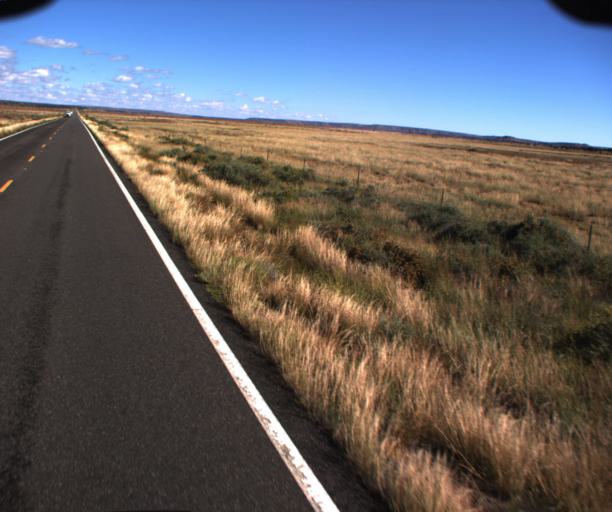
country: US
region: Arizona
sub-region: Apache County
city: Saint Johns
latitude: 34.6862
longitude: -109.2792
